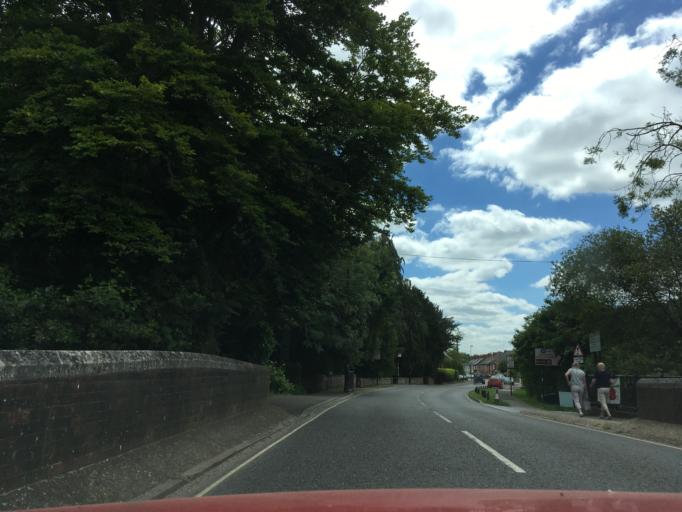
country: GB
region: England
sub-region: Hampshire
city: Overton
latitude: 51.2283
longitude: -1.3383
